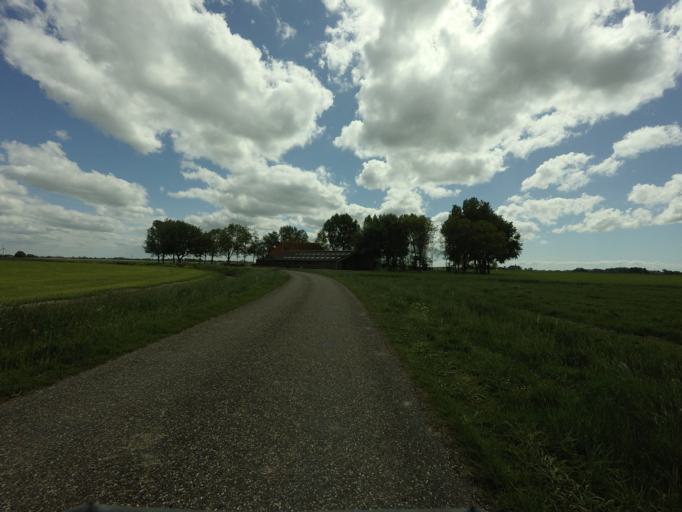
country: NL
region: Friesland
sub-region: Gemeente Franekeradeel
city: Tzum
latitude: 53.1373
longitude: 5.5578
